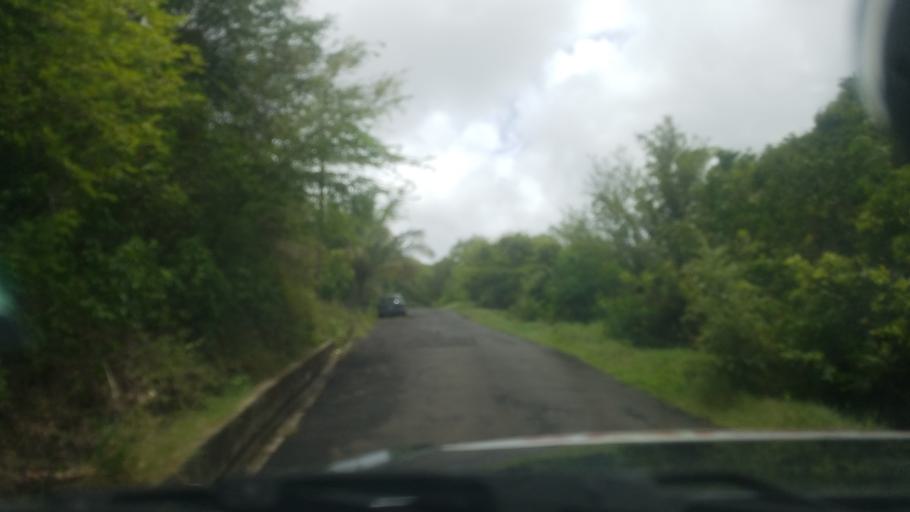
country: LC
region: Laborie Quarter
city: Laborie
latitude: 13.7442
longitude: -60.9641
